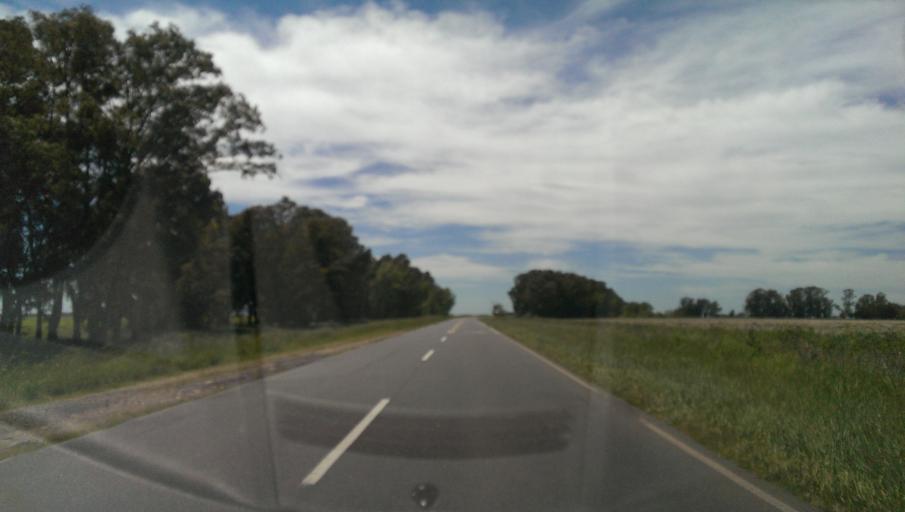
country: AR
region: Buenos Aires
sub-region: Partido de Laprida
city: Laprida
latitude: -37.2489
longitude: -60.8131
